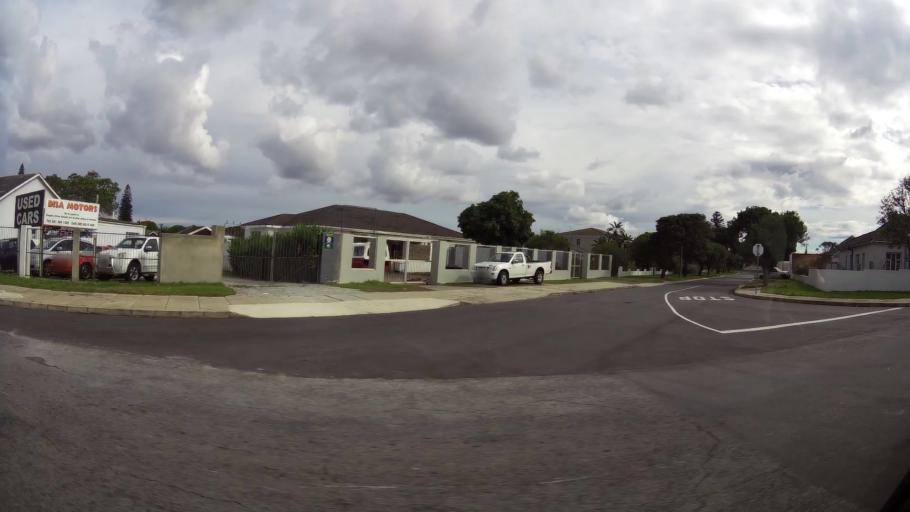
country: ZA
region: Eastern Cape
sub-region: Nelson Mandela Bay Metropolitan Municipality
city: Port Elizabeth
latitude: -33.9461
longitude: 25.5543
